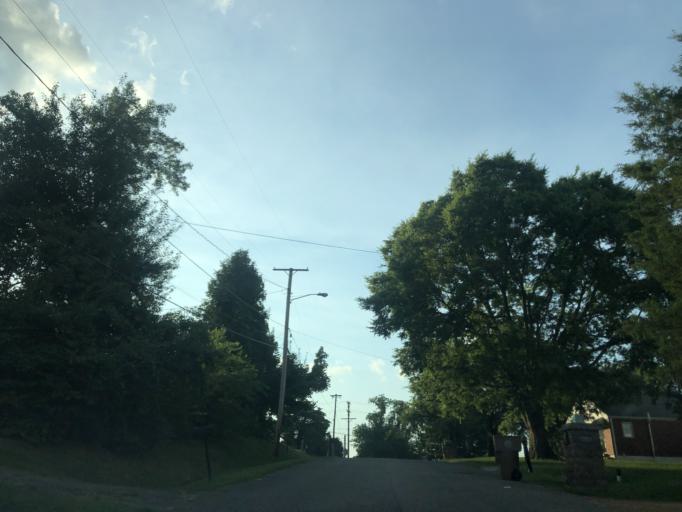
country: US
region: Tennessee
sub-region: Davidson County
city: Nashville
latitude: 36.1566
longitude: -86.7066
